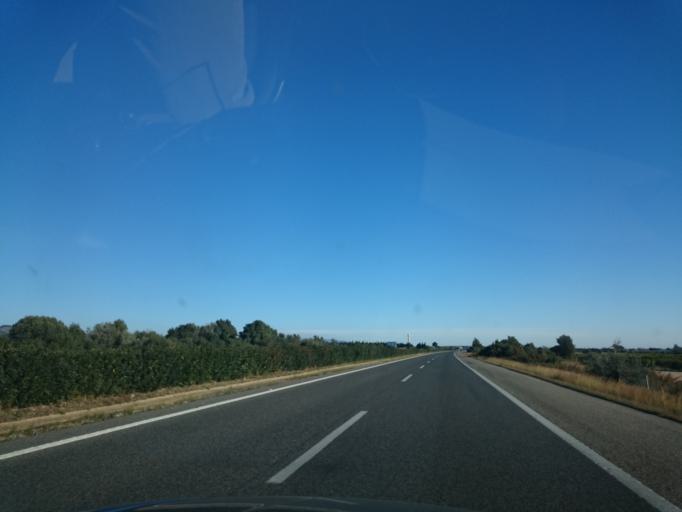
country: ES
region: Catalonia
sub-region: Provincia de Tarragona
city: Camarles
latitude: 40.7837
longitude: 0.6510
